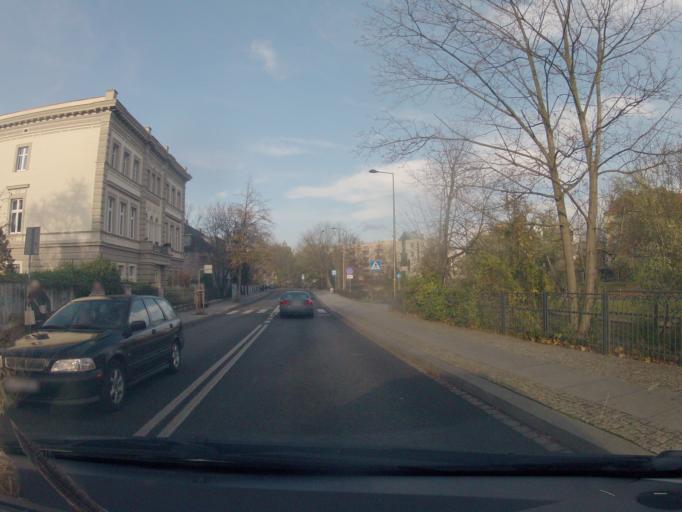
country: PL
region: Opole Voivodeship
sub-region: Powiat opolski
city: Opole
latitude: 50.6631
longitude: 17.9220
